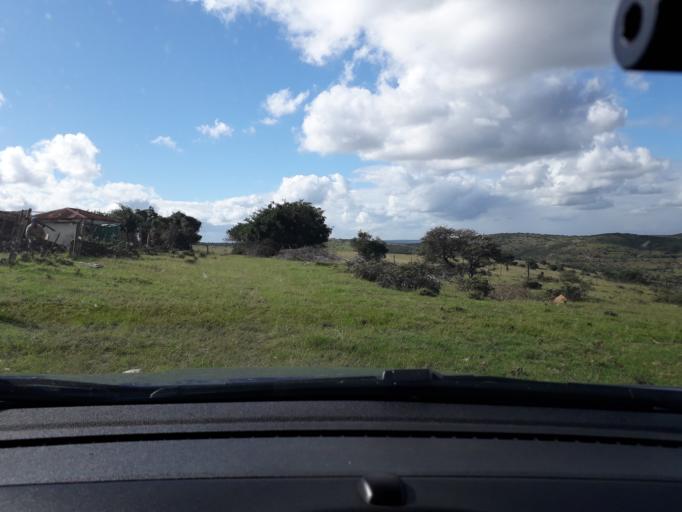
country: ZA
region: Eastern Cape
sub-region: Buffalo City Metropolitan Municipality
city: Bhisho
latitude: -33.1122
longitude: 27.4315
